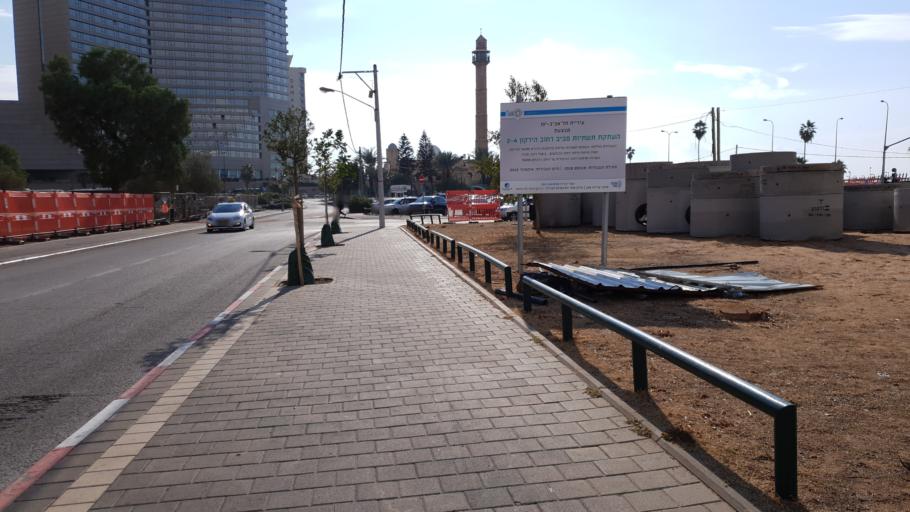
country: IL
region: Tel Aviv
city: Tel Aviv
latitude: 32.0675
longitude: 34.7645
